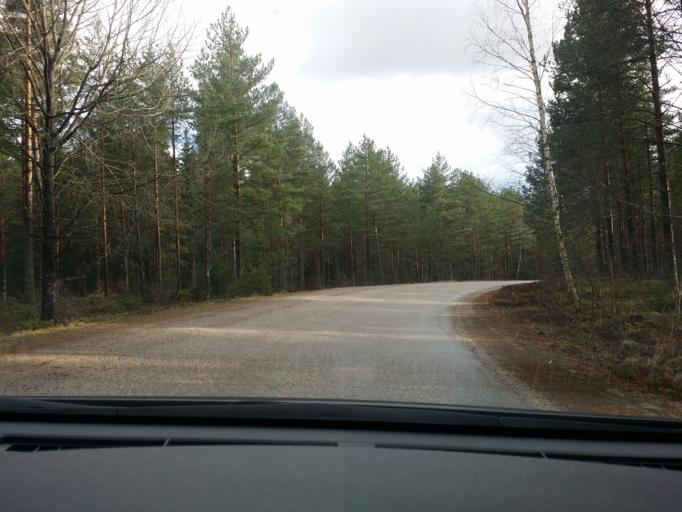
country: SE
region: Soedermanland
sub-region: Eskilstuna Kommun
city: Arla
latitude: 59.3286
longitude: 16.6858
